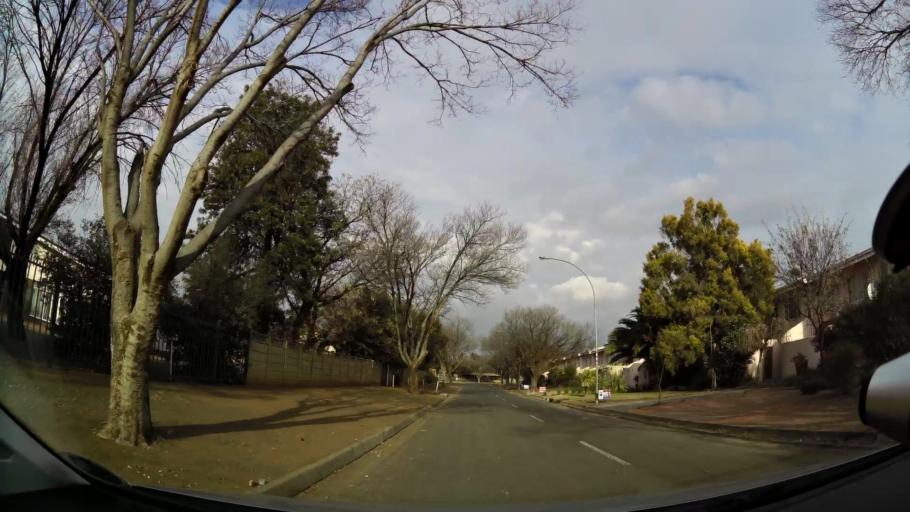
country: ZA
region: Orange Free State
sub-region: Mangaung Metropolitan Municipality
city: Bloemfontein
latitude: -29.1207
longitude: 26.1760
